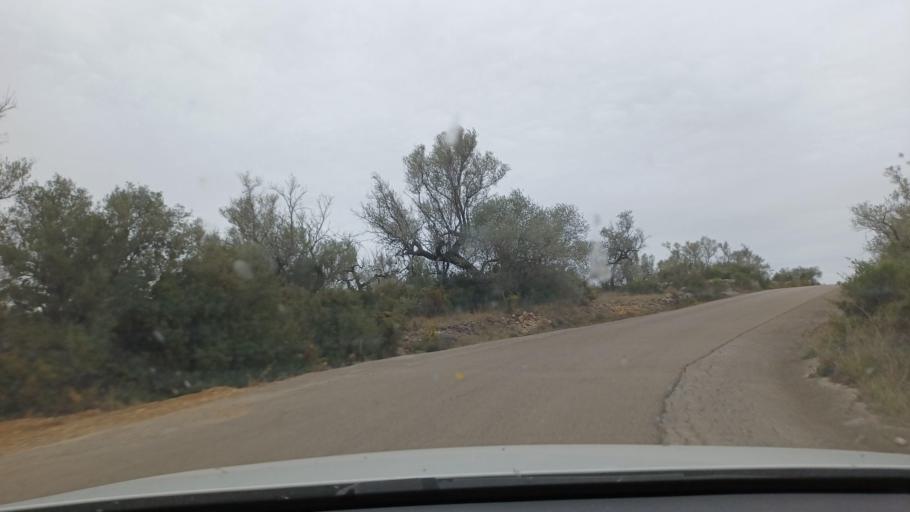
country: ES
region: Valencia
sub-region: Provincia de Castello
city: Canet lo Roig
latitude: 40.5782
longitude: 0.2824
